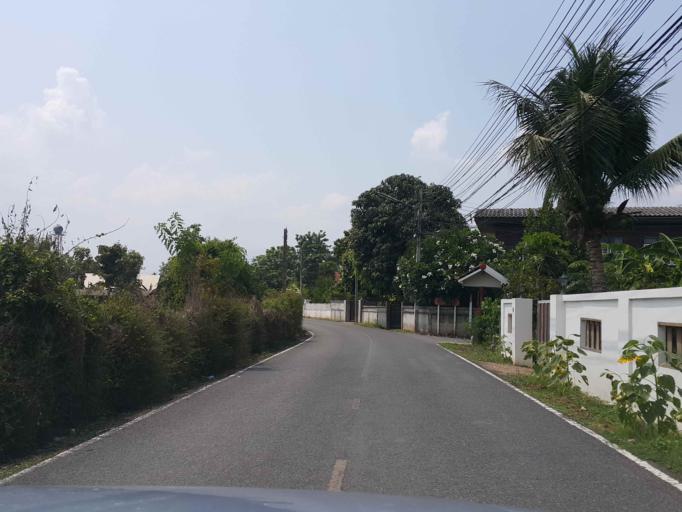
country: TH
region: Chiang Mai
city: Saraphi
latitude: 18.6940
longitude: 98.9875
